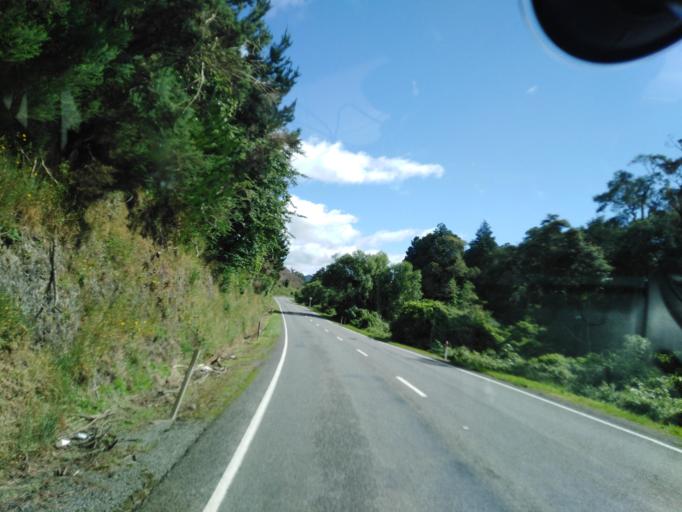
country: NZ
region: Nelson
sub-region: Nelson City
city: Nelson
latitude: -41.2583
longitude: 173.5757
